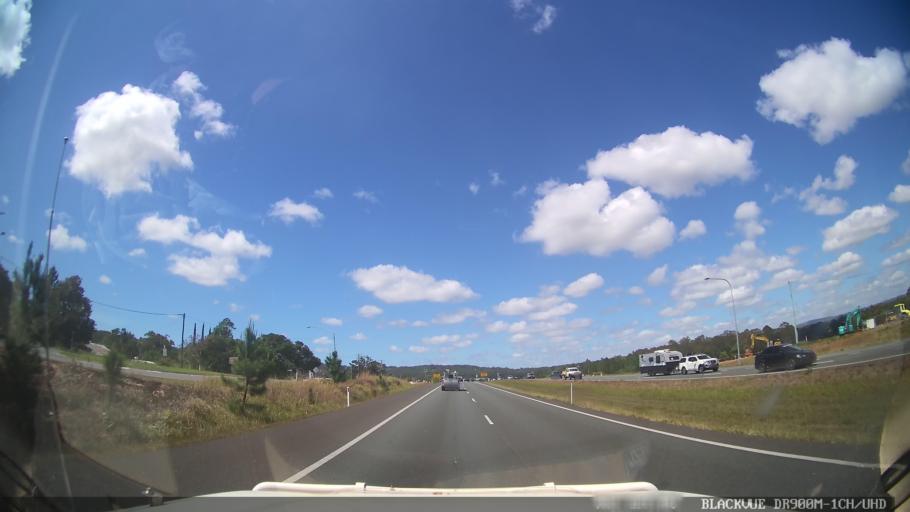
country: AU
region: Queensland
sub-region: Sunshine Coast
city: Woombye
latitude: -26.6839
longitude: 153.0032
